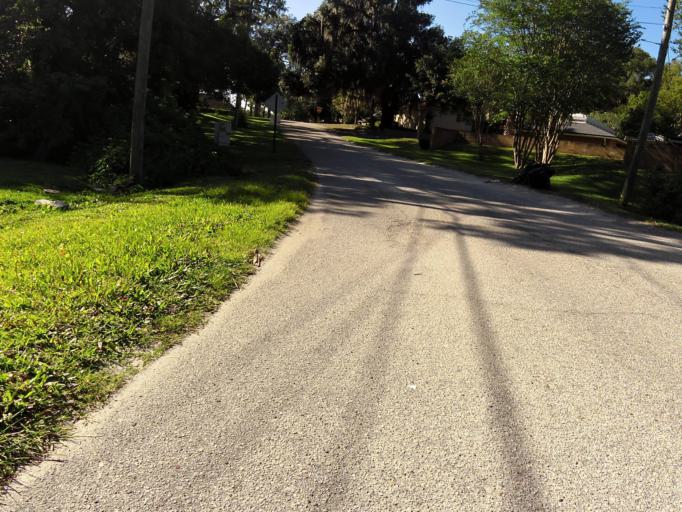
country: US
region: Florida
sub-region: Duval County
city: Jacksonville
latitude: 30.3129
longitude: -81.6174
